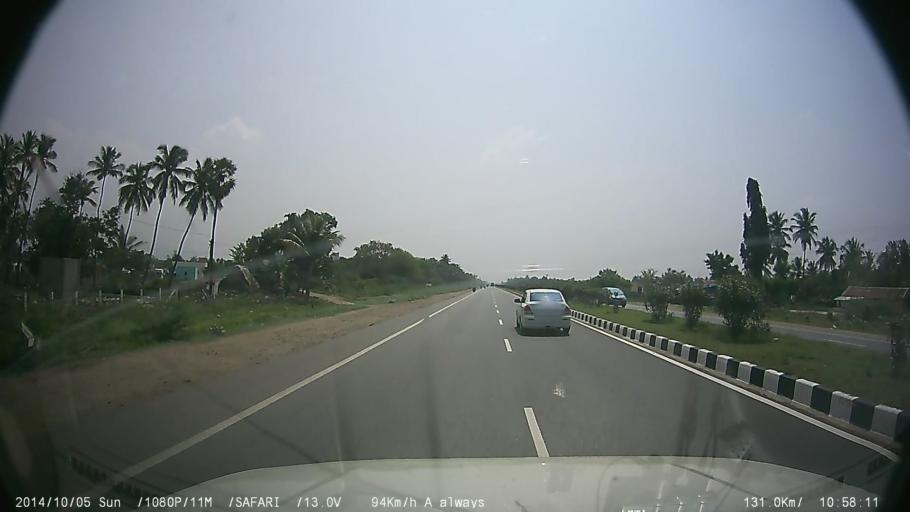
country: IN
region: Tamil Nadu
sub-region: Salem
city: Attur
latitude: 11.6461
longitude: 78.5133
